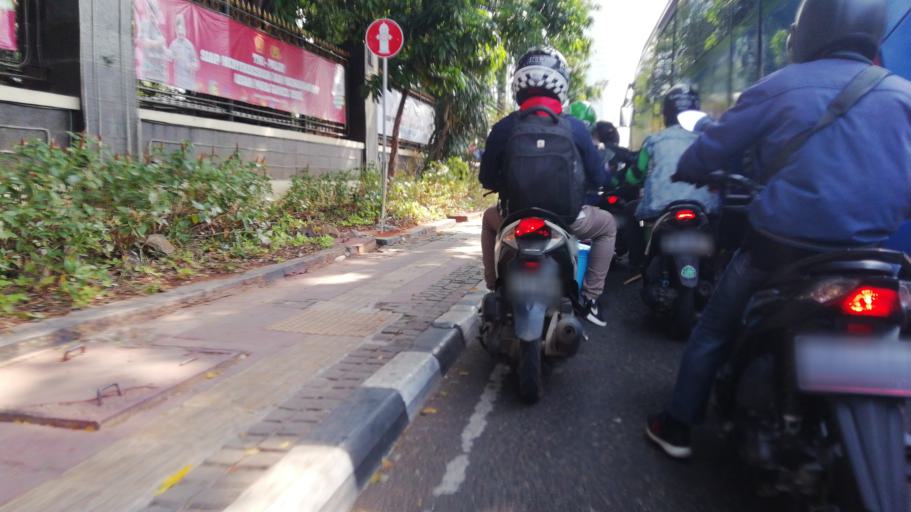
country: ID
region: Jakarta Raya
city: Jakarta
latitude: -6.2210
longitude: 106.8108
